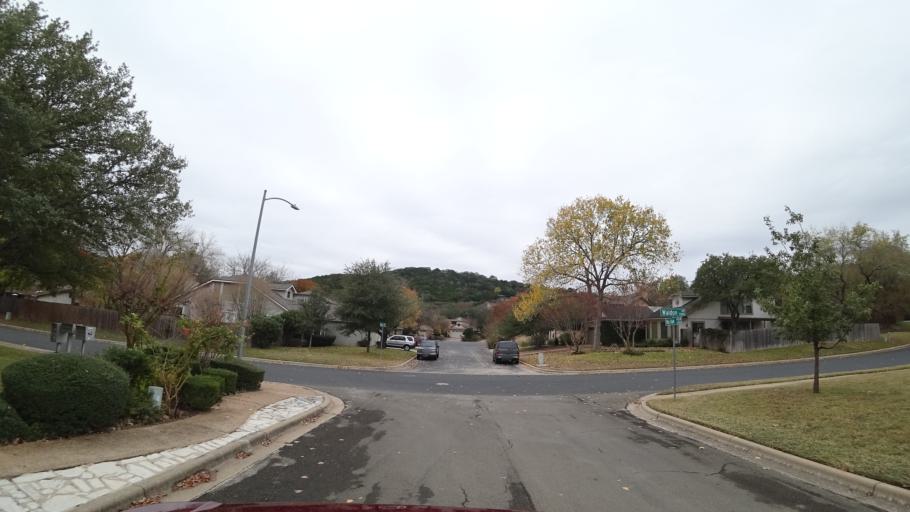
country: US
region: Texas
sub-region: Williamson County
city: Jollyville
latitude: 30.3755
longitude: -97.7867
